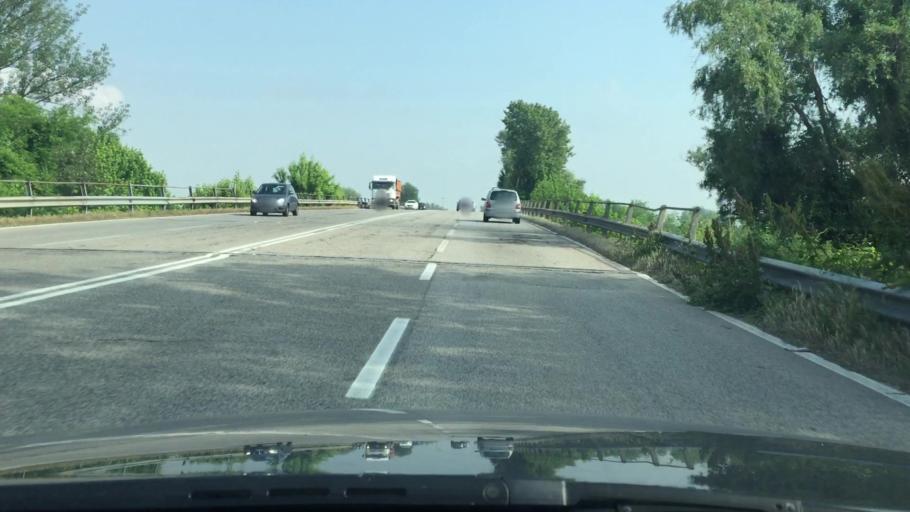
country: IT
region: Emilia-Romagna
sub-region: Provincia di Ferrara
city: Gaibanella-Sant'Edigio
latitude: 44.8000
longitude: 11.6368
